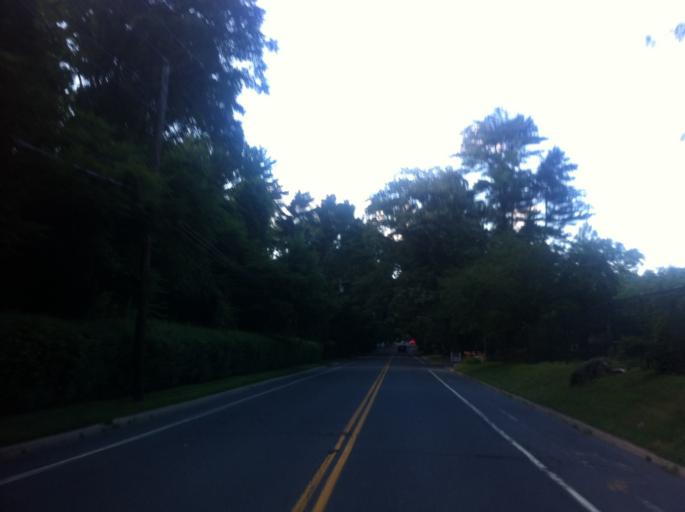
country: US
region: New York
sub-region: Nassau County
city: Locust Valley
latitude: 40.8870
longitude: -73.5858
